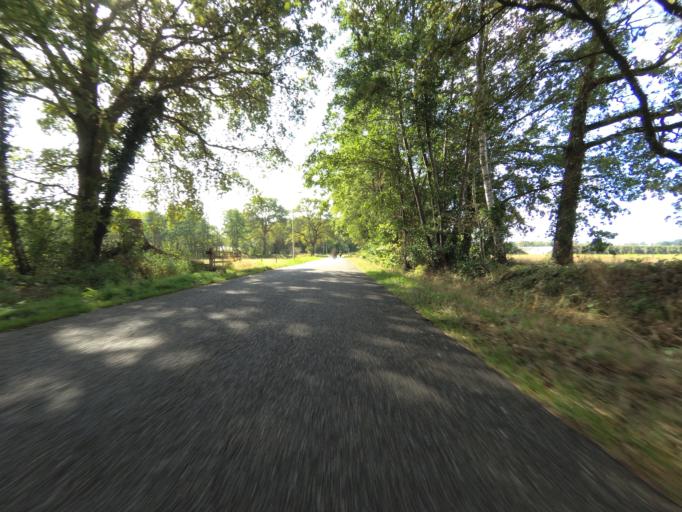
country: NL
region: Overijssel
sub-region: Gemeente Haaksbergen
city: Haaksbergen
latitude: 52.1901
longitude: 6.8003
